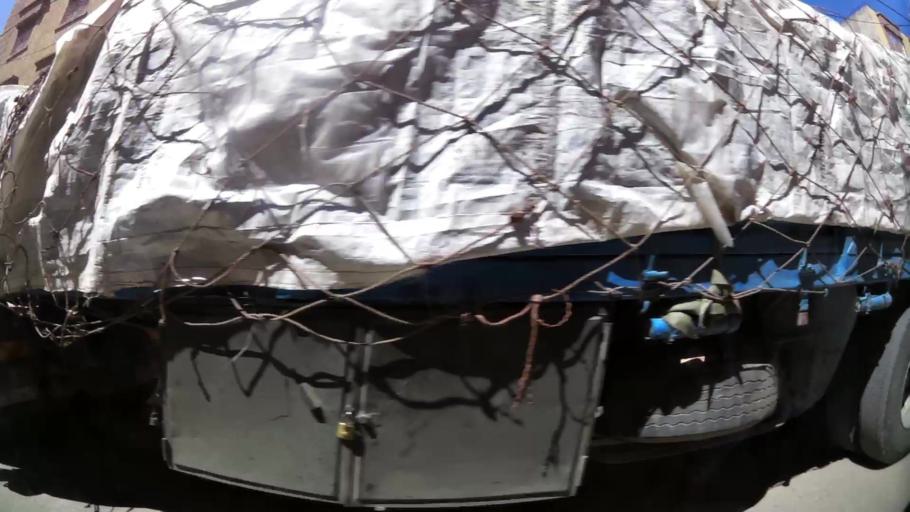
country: MA
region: Oriental
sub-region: Oujda-Angad
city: Oujda
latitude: 34.6874
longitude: -1.9361
